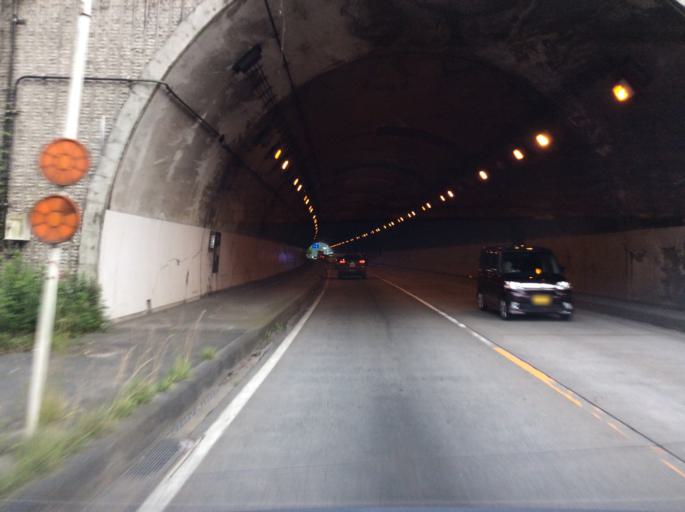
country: JP
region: Fukushima
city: Iwaki
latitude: 37.0313
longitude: 140.8790
